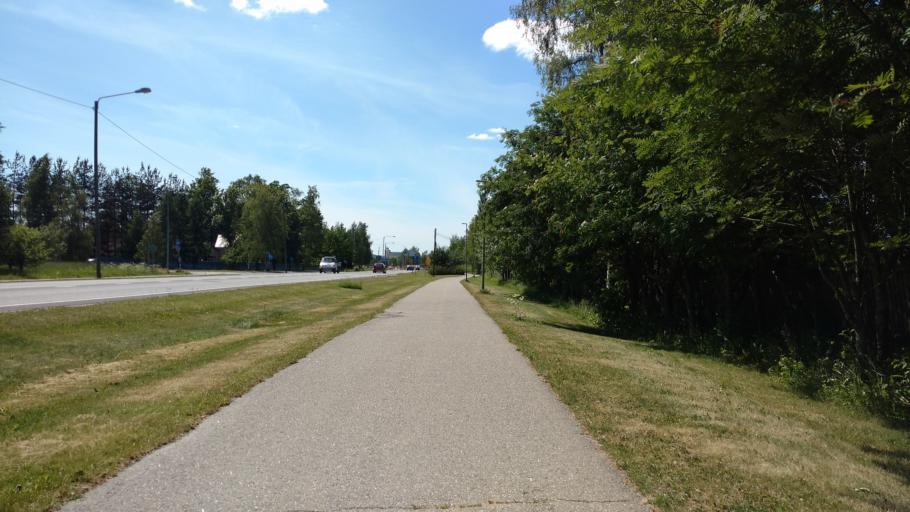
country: FI
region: Varsinais-Suomi
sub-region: Salo
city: Salo
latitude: 60.3969
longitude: 23.1368
